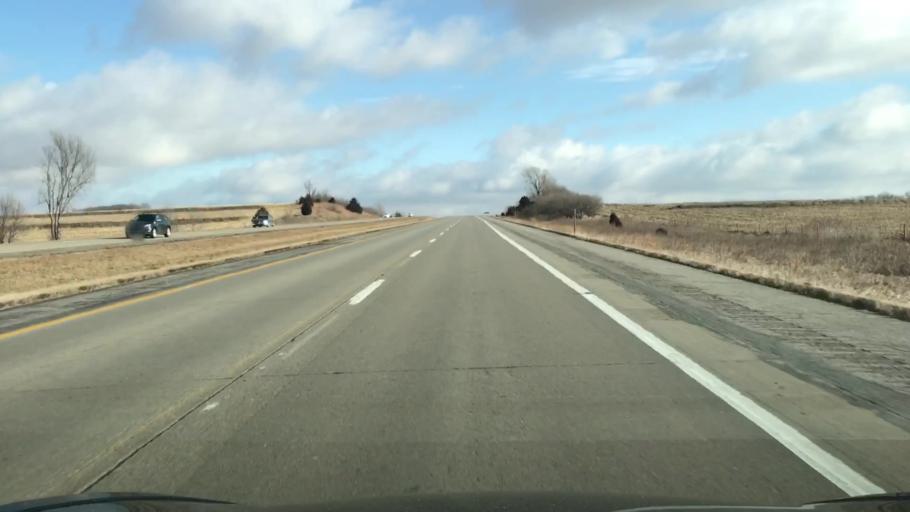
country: US
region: Iowa
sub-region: Cass County
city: Atlantic
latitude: 41.4971
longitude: -94.8571
